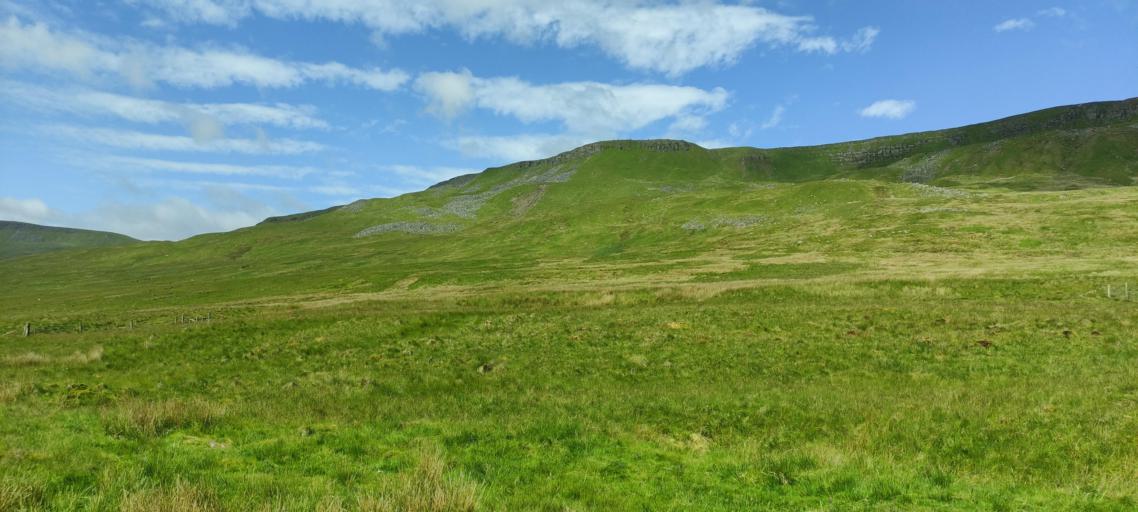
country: GB
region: England
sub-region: Cumbria
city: Kirkby Stephen
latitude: 54.3836
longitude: -2.3520
